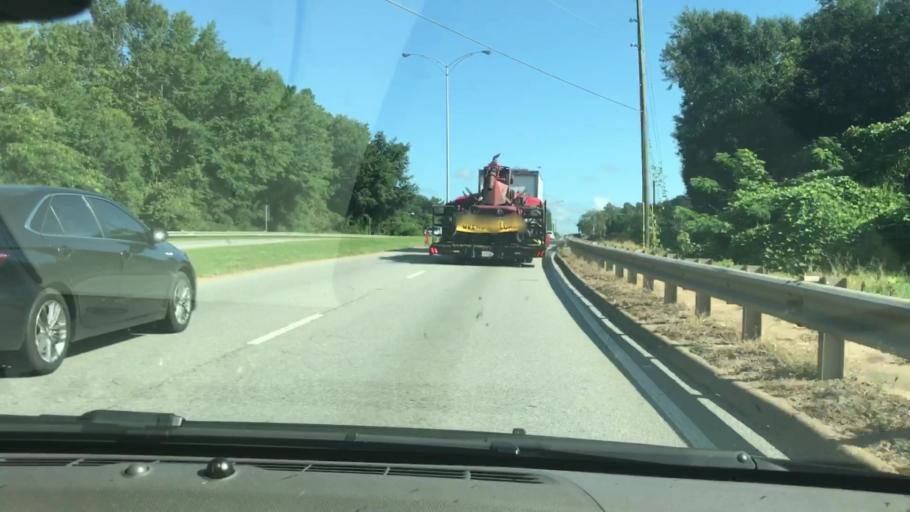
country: US
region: Alabama
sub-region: Barbour County
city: Eufaula
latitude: 31.9078
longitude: -85.1493
